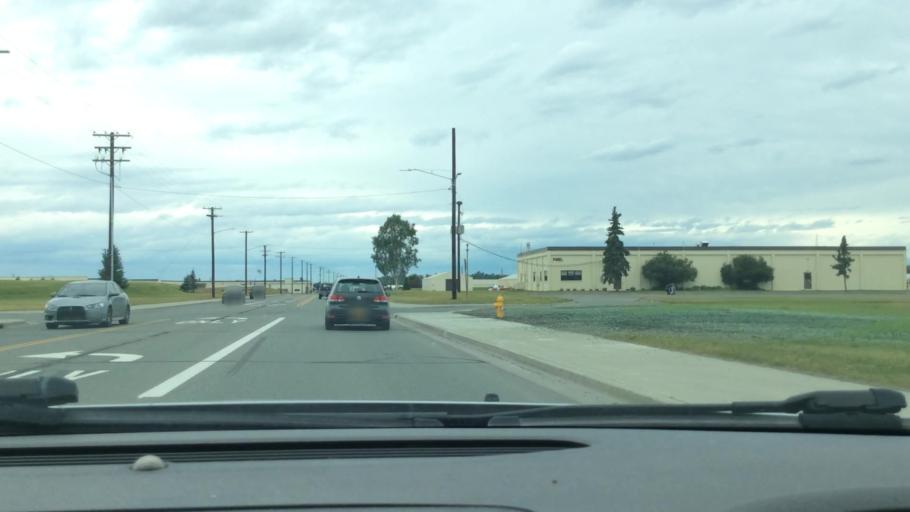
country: US
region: Alaska
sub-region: Anchorage Municipality
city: Anchorage
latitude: 61.2374
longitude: -149.8341
